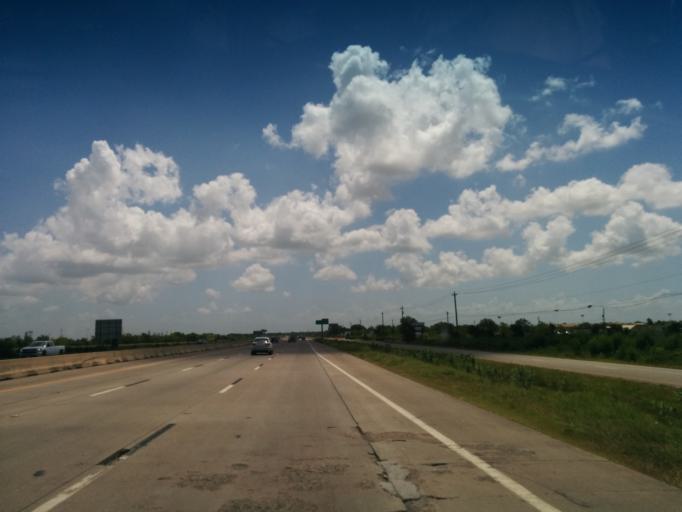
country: US
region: Texas
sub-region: Harris County
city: Baytown
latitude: 29.8091
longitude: -94.9569
